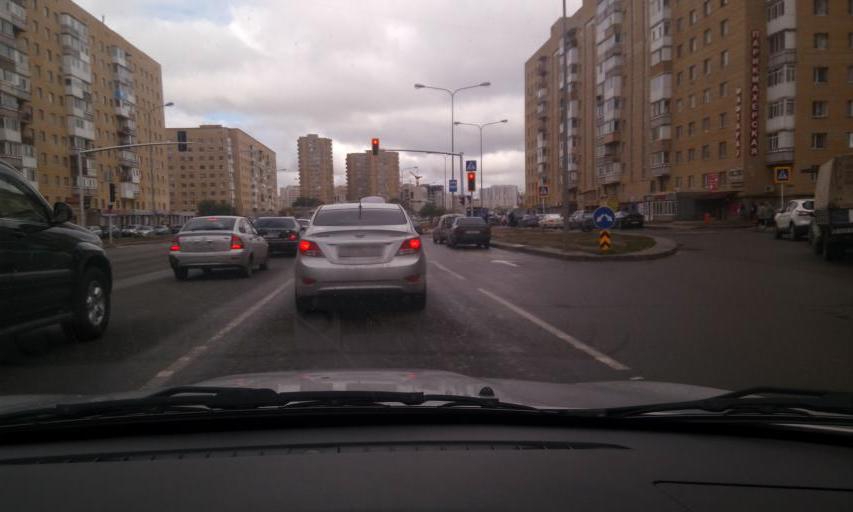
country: KZ
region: Astana Qalasy
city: Astana
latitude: 51.1710
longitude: 71.3841
